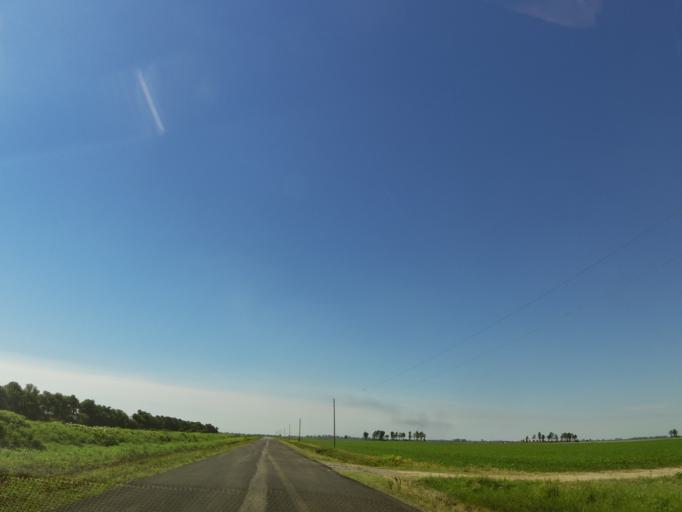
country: US
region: Missouri
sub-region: New Madrid County
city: Lilbourn
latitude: 36.5648
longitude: -89.7028
